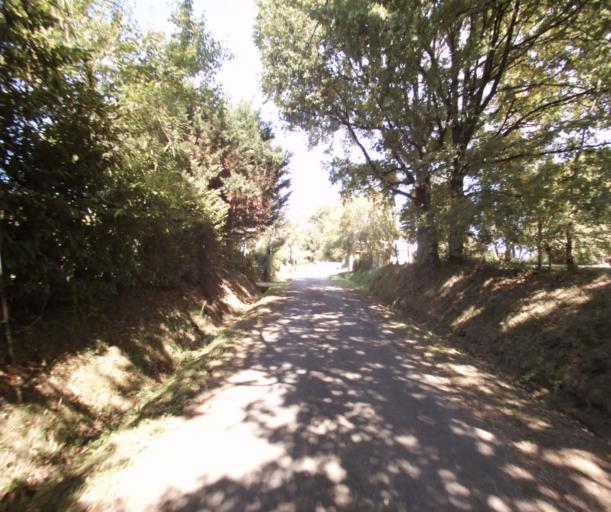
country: FR
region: Midi-Pyrenees
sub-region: Departement du Gers
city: Cazaubon
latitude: 43.9479
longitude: -0.0599
